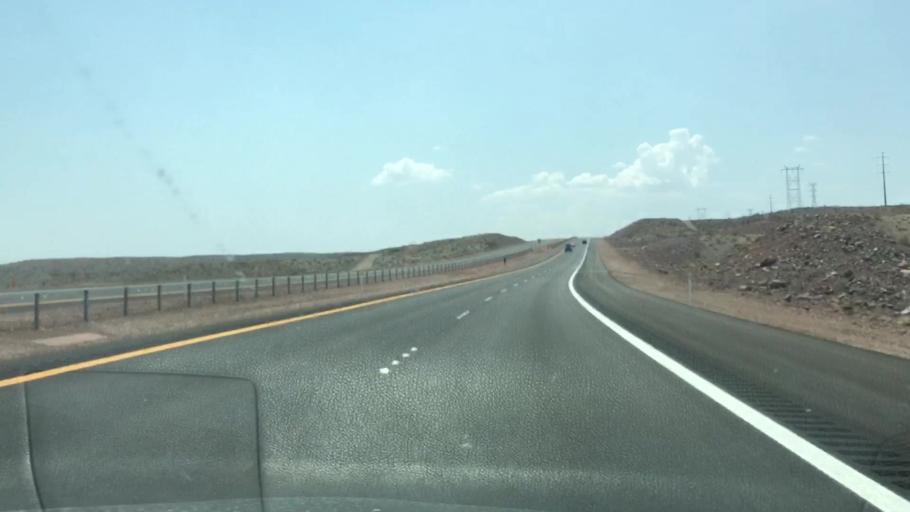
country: US
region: Nevada
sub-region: Clark County
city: Boulder City
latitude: 35.9743
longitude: -114.7932
